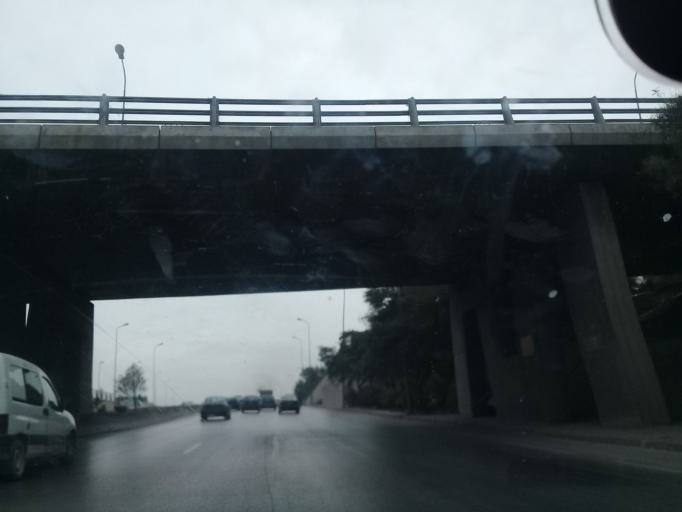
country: TN
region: Tunis
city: Tunis
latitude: 36.8334
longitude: 10.1557
